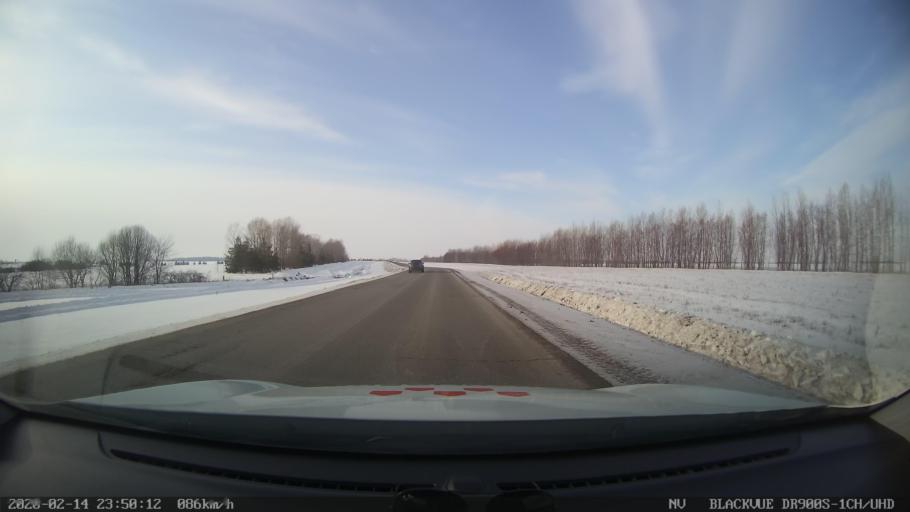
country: RU
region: Tatarstan
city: Kuybyshevskiy Zaton
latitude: 55.2582
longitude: 49.1671
